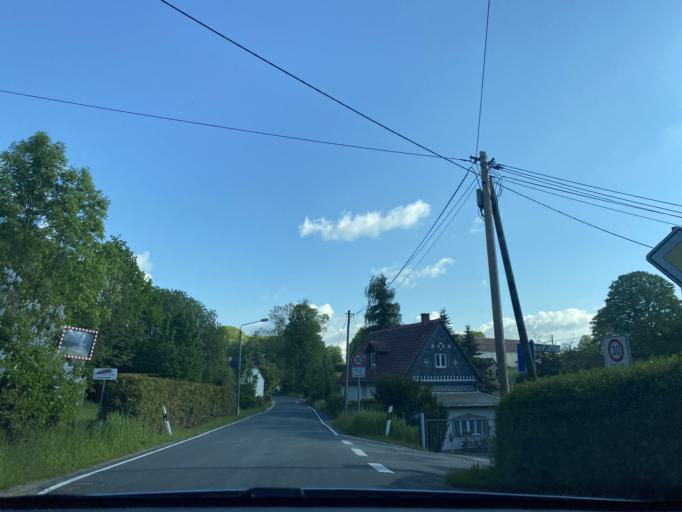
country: DE
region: Saxony
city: Markersdorf
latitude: 51.1423
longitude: 14.9241
